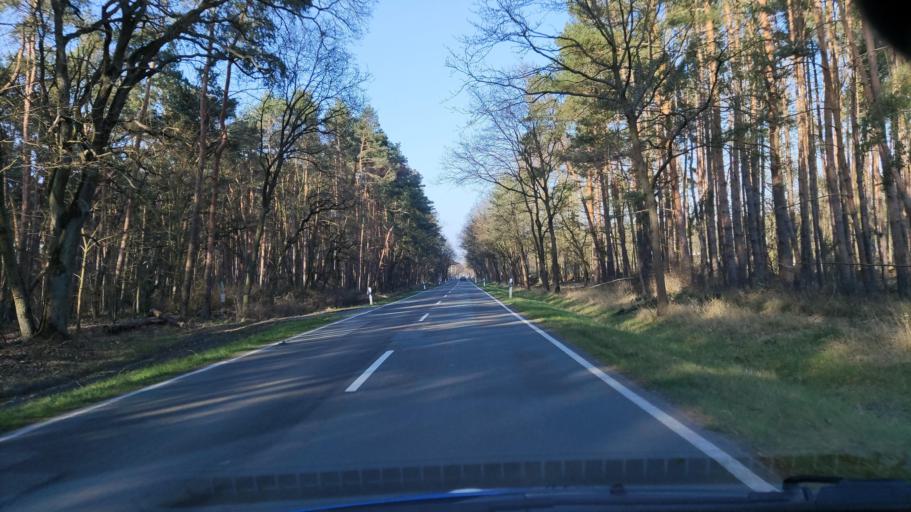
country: DE
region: Saxony-Anhalt
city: Seehausen
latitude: 52.8703
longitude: 11.7396
